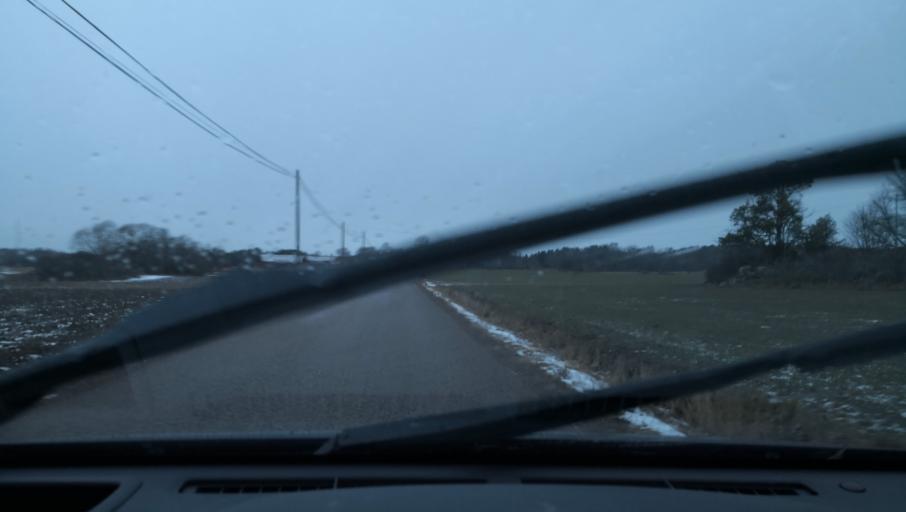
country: SE
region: Soedermanland
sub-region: Strangnas Kommun
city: Strangnas
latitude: 59.4509
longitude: 16.8674
